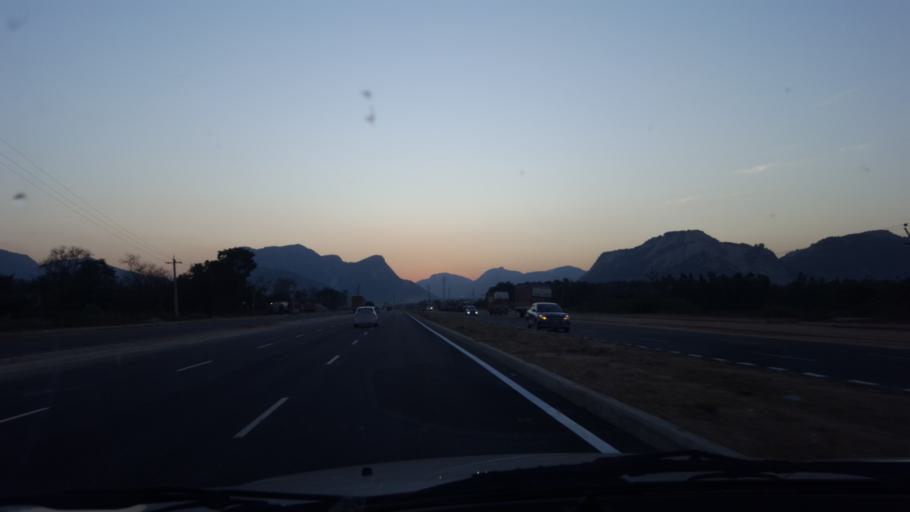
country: IN
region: Andhra Pradesh
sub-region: Chittoor
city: Narasingapuram
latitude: 13.5840
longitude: 79.3266
